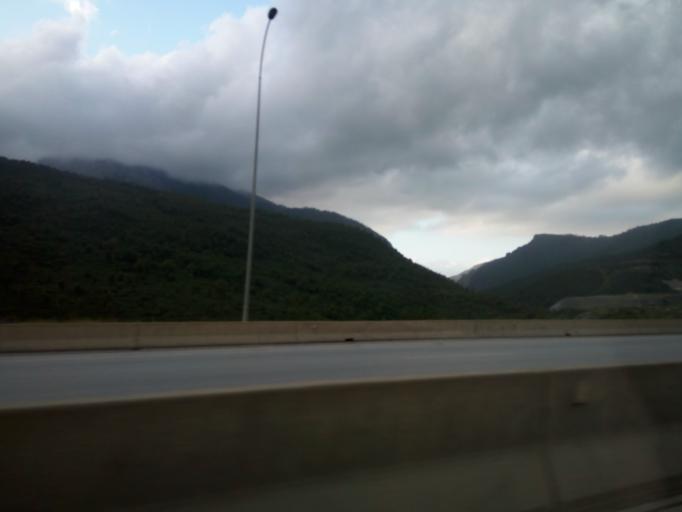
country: DZ
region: Boumerdes
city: Arbatache
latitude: 36.5800
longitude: 3.4545
